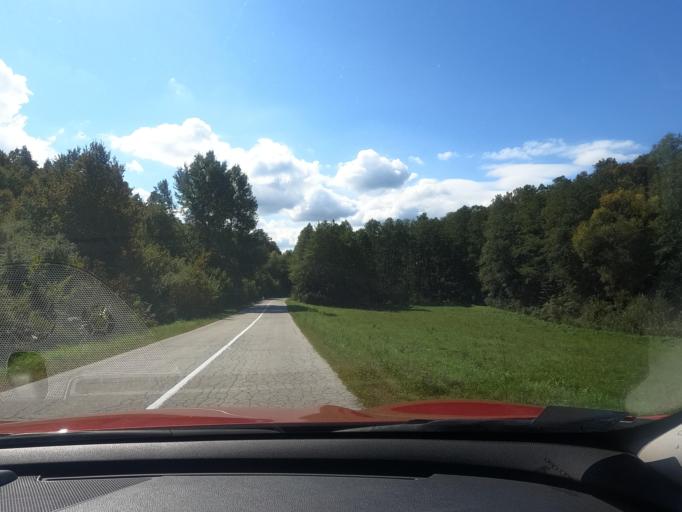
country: BA
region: Federation of Bosnia and Herzegovina
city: Podzvizd
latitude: 45.2290
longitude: 15.8879
